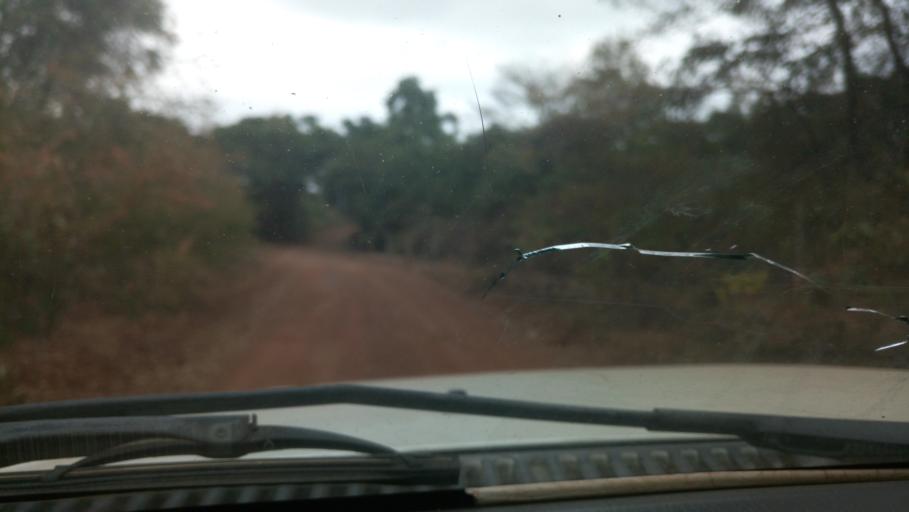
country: KE
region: Nairobi Area
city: Nairobi
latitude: -1.3674
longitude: 36.7682
